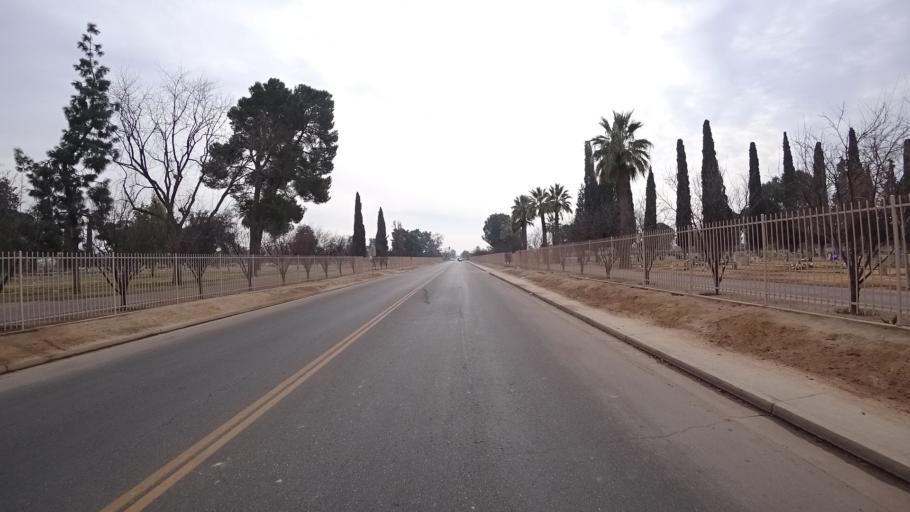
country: US
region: California
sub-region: Kern County
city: Bakersfield
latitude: 35.3636
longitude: -118.9941
